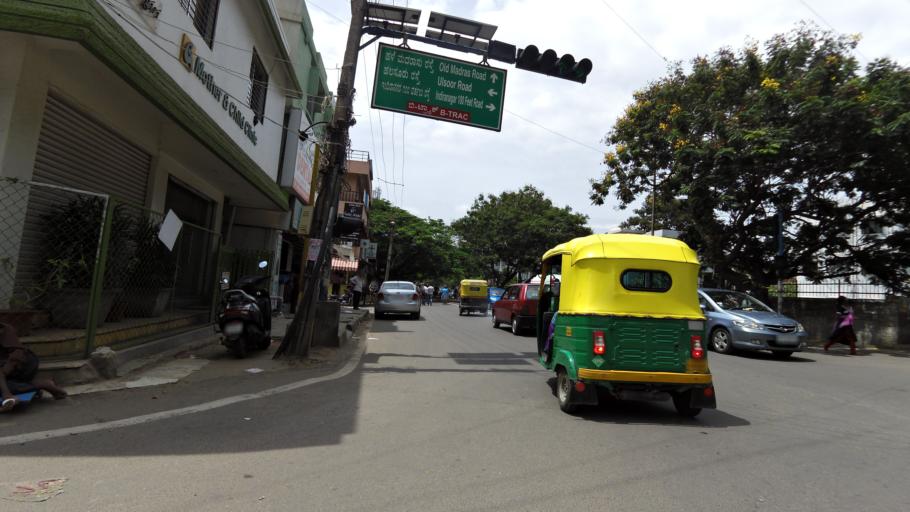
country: IN
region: Karnataka
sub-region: Bangalore Urban
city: Bangalore
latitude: 12.9717
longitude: 77.6359
